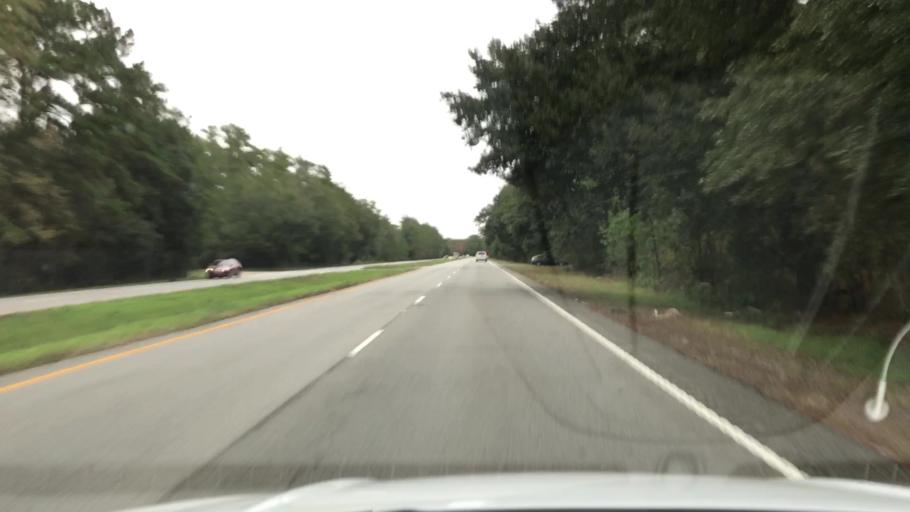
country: US
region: South Carolina
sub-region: Georgetown County
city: Georgetown
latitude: 33.3971
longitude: -79.2016
